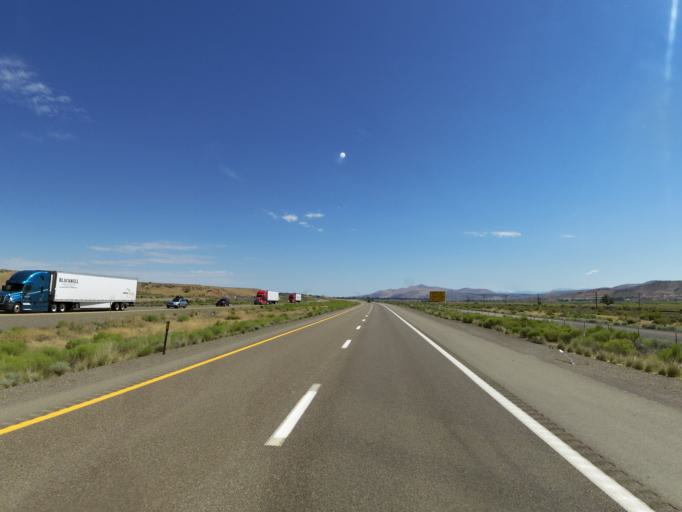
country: US
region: Nevada
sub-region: Elko County
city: Elko
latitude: 40.8025
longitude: -115.8332
